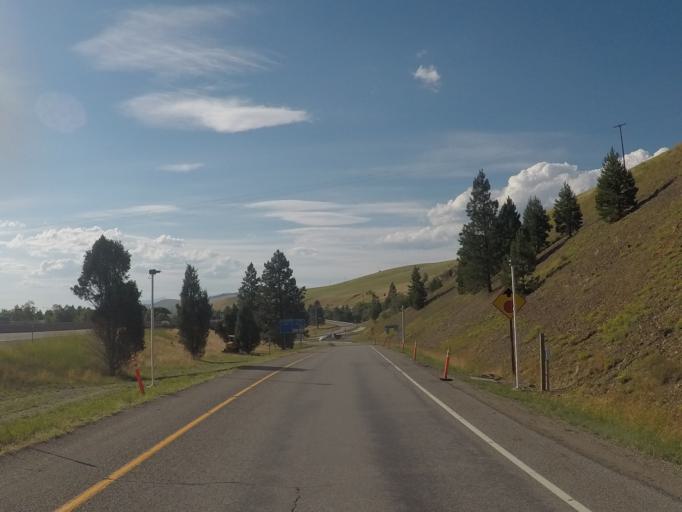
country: US
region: Montana
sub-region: Missoula County
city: Missoula
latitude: 46.8791
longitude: -113.9910
